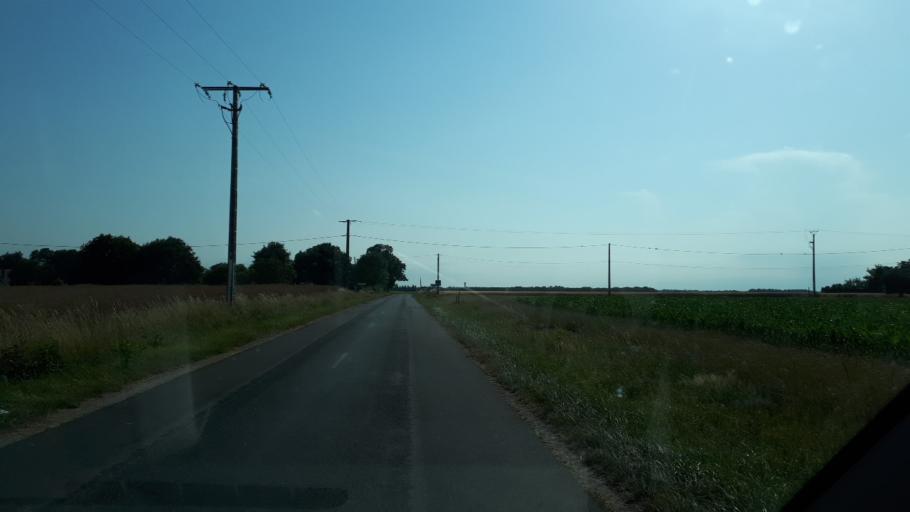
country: FR
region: Centre
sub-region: Departement du Loir-et-Cher
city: La Ville-aux-Clercs
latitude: 47.9102
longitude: 1.0661
